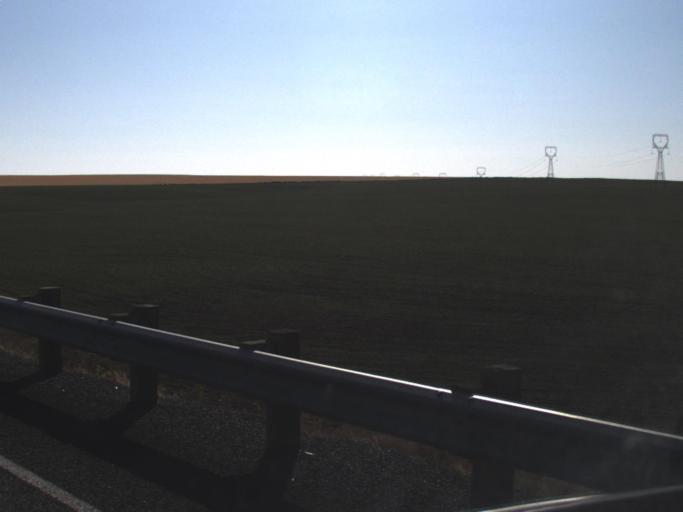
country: US
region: Washington
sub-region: Franklin County
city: Connell
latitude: 46.6201
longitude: -118.7011
